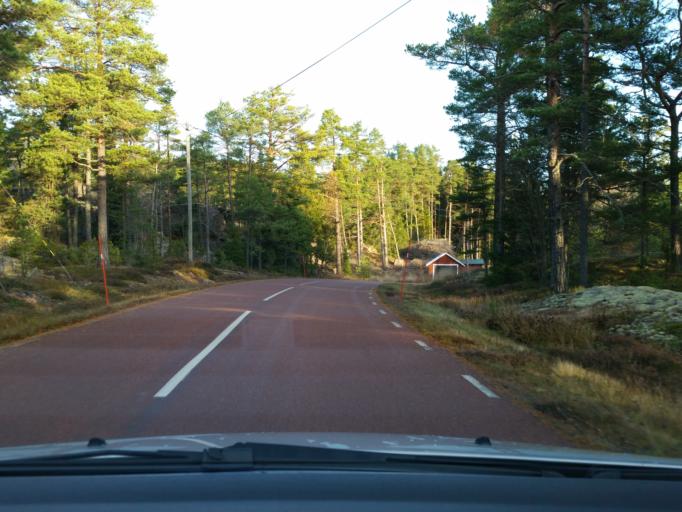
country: AX
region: Alands landsbygd
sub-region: Sund
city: Sund
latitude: 60.3095
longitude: 20.1906
